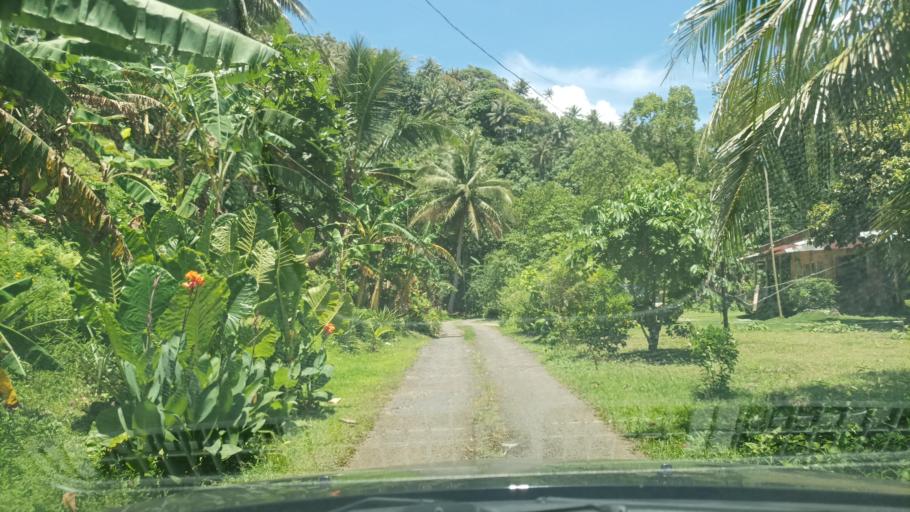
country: FM
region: Kosrae
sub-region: Lelu Municipality
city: Lelu
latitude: 5.3294
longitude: 163.0325
